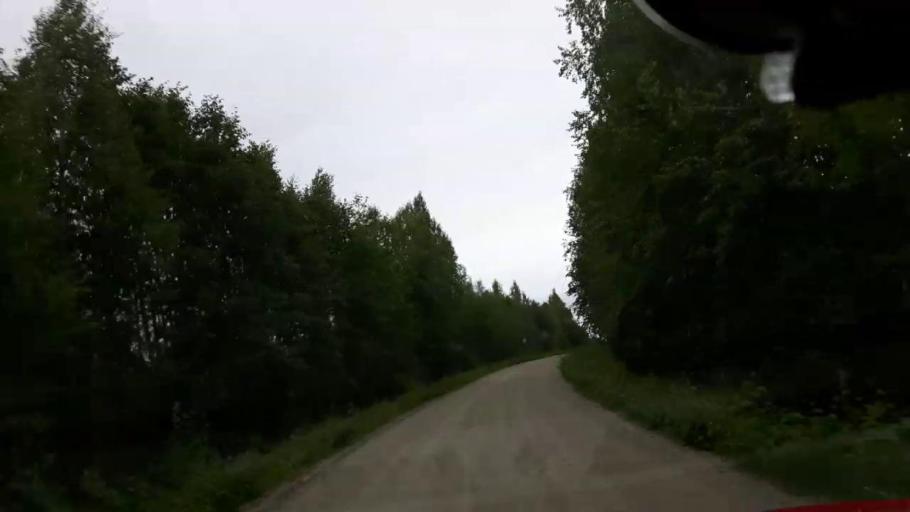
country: SE
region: Vaesternorrland
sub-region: Ange Kommun
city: Ange
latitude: 62.8015
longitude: 15.7699
